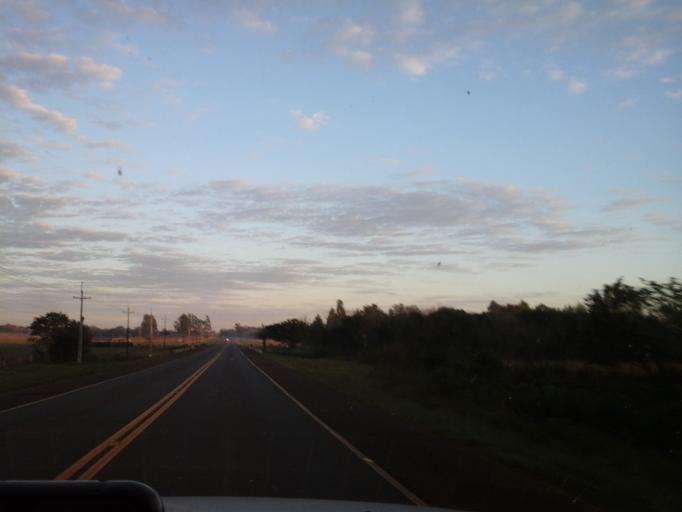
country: PY
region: Misiones
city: Santiago
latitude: -27.0414
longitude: -56.6616
